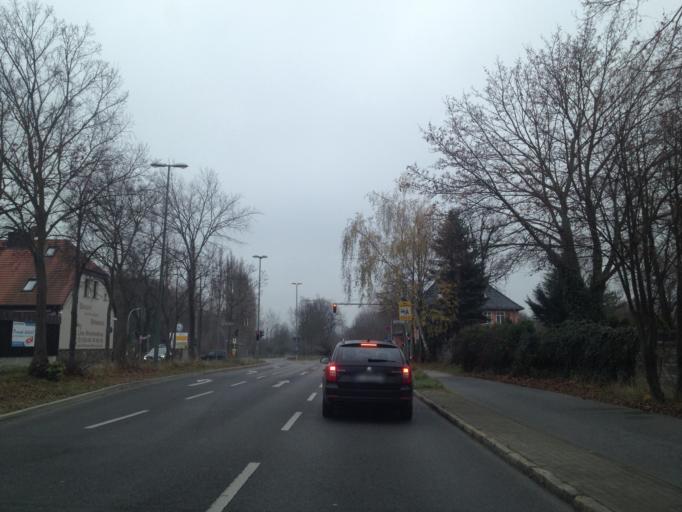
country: DE
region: Berlin
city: Blankenfelde
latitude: 52.6193
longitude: 13.3899
